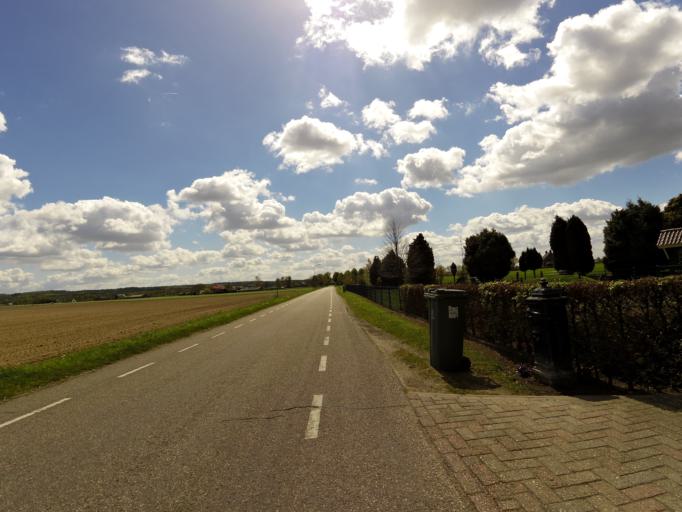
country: NL
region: Gelderland
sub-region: Gemeente Montferland
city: s-Heerenberg
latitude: 51.9405
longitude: 6.2023
